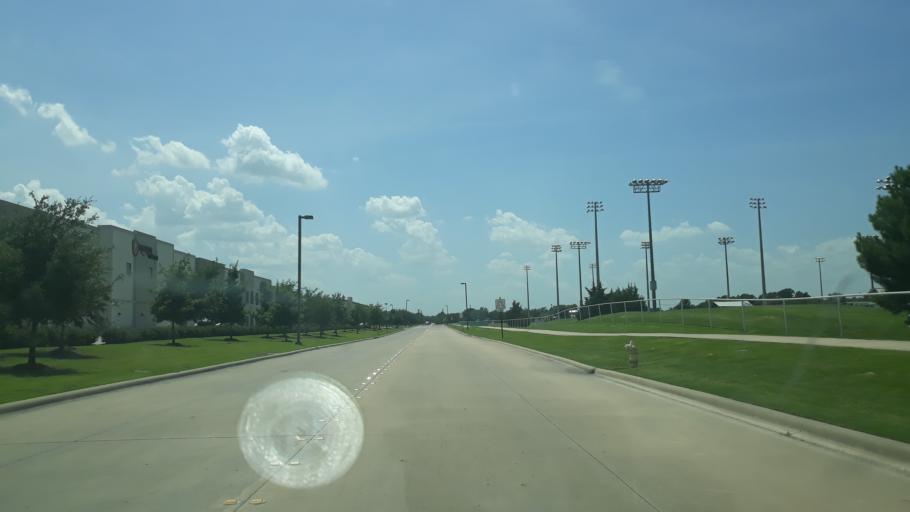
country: US
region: Texas
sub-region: Dallas County
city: Coppell
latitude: 32.9610
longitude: -97.0161
